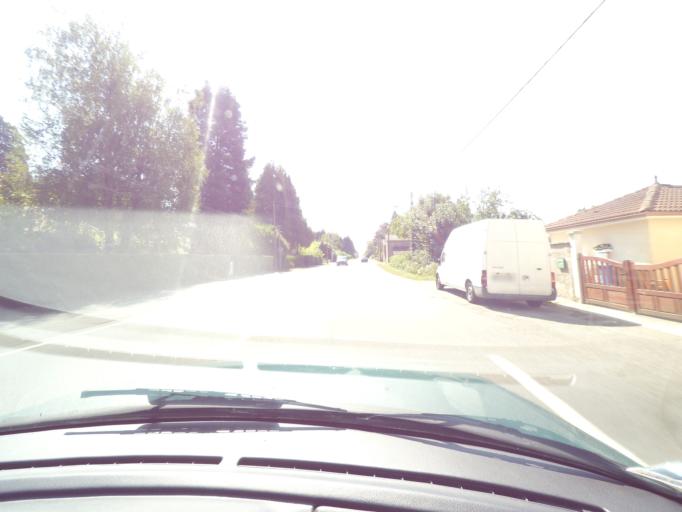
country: FR
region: Limousin
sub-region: Departement de la Haute-Vienne
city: Couzeix
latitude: 45.8957
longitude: 1.2300
